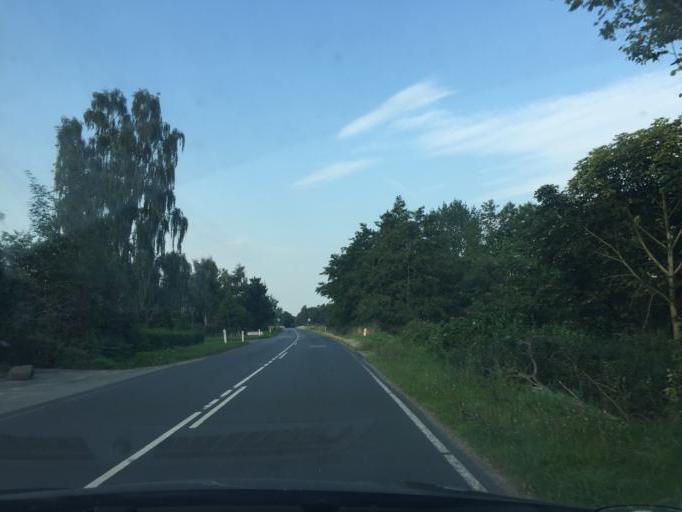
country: DK
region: South Denmark
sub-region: Kerteminde Kommune
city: Langeskov
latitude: 55.2949
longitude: 10.5690
